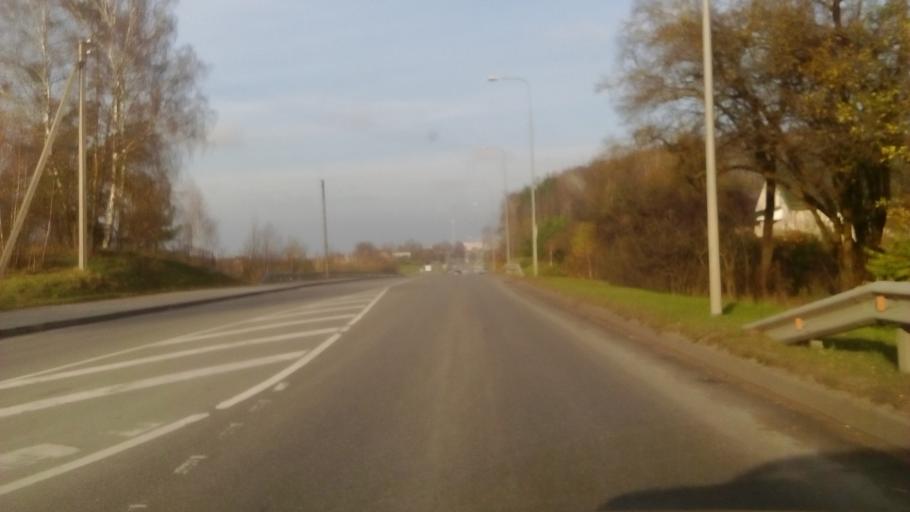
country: LT
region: Alytaus apskritis
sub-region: Alytus
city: Alytus
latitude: 54.4009
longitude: 24.0012
